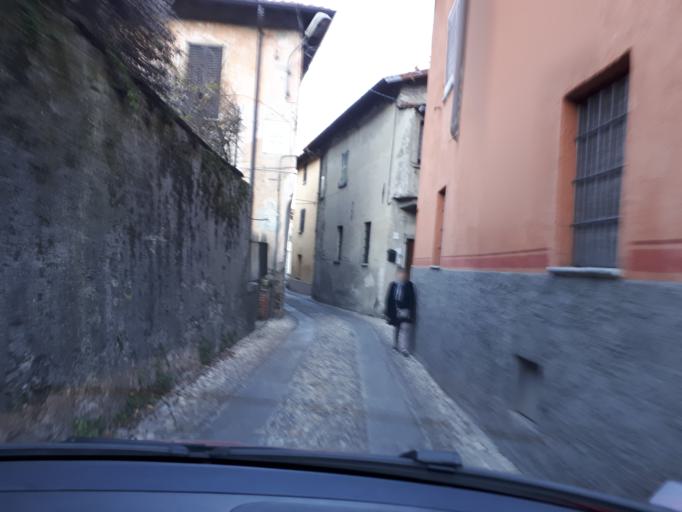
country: IT
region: Lombardy
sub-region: Provincia di Como
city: Bellagio
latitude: 45.9745
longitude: 9.2611
